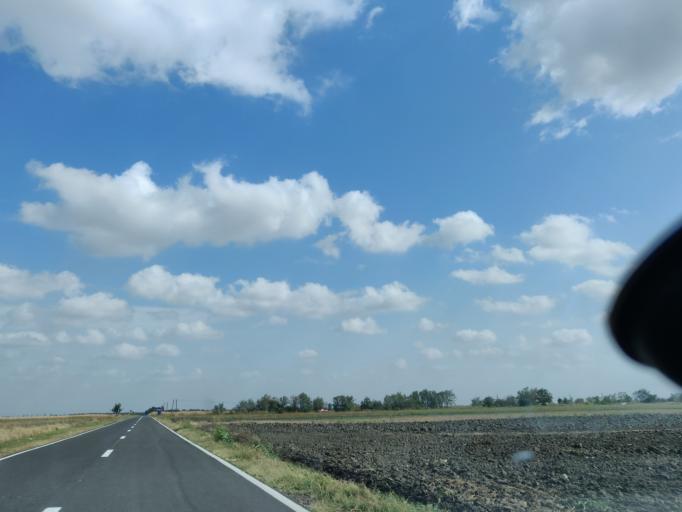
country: RO
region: Vrancea
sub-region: Comuna Maicanesti
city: Ramniceni
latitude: 45.4687
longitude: 27.4246
